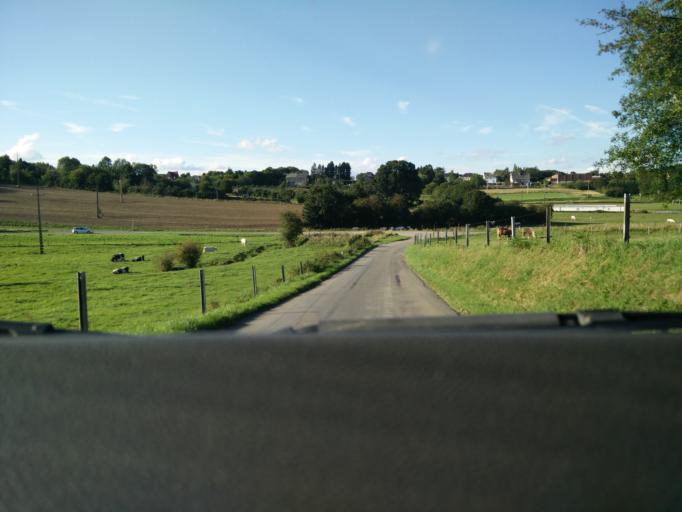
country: BE
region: Wallonia
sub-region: Province du Hainaut
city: Beaumont
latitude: 50.2324
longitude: 4.2458
